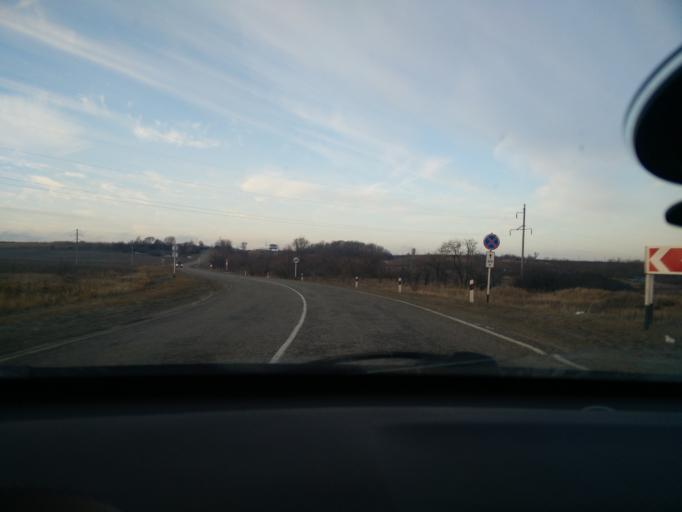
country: RU
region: Stavropol'skiy
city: Balakhonovskoye
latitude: 44.9842
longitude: 41.6967
